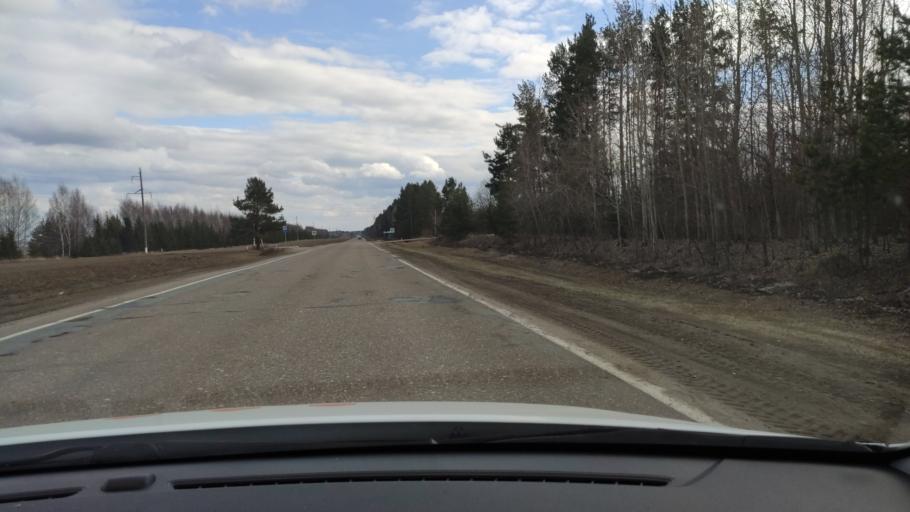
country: RU
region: Tatarstan
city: Vysokaya Gora
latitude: 56.0587
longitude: 49.2067
